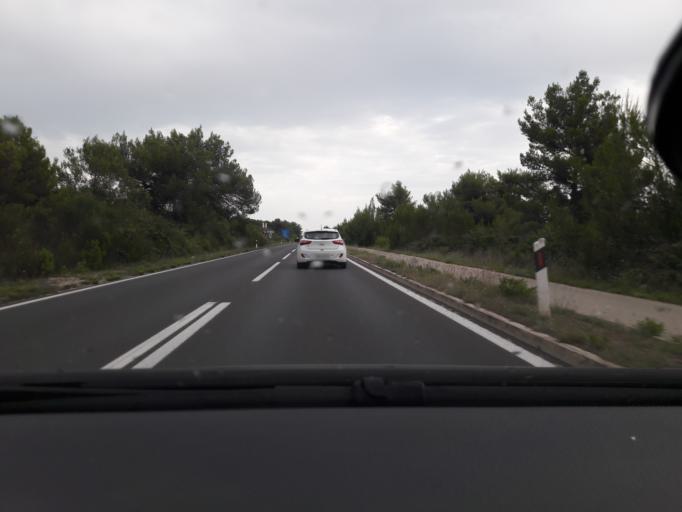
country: HR
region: Zadarska
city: Nin
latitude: 44.1890
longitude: 15.1817
